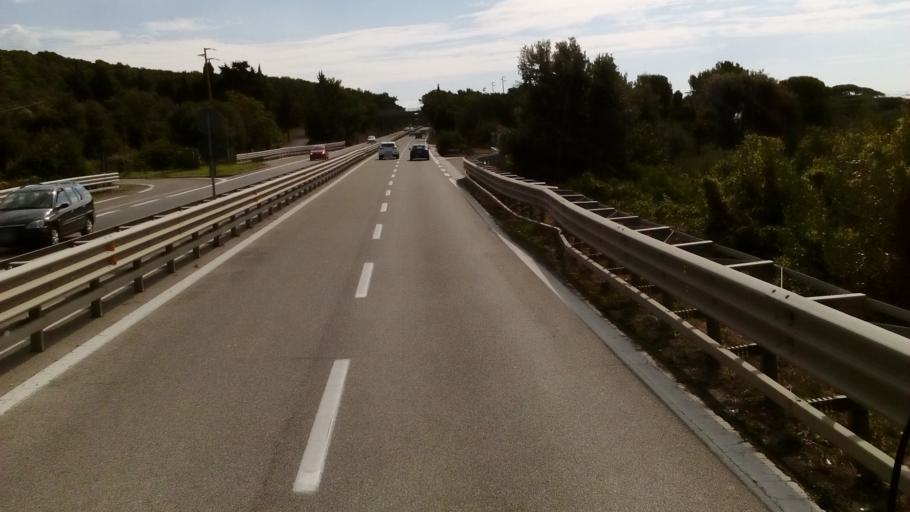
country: IT
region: Tuscany
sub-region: Provincia di Livorno
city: Quercianella
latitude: 43.4390
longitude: 10.3878
